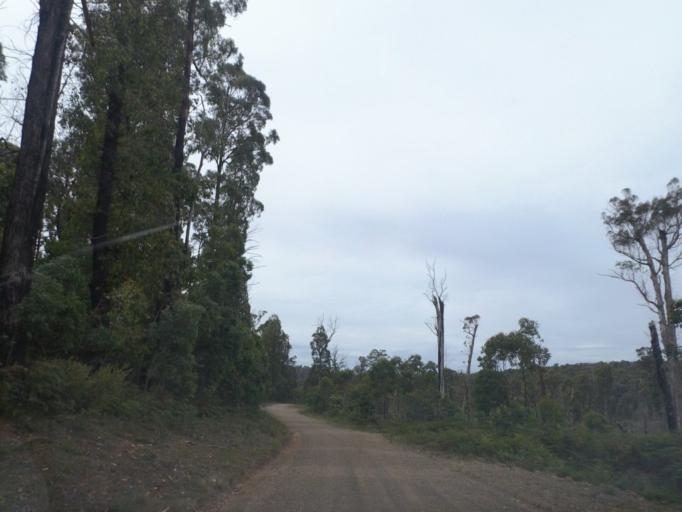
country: AU
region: Victoria
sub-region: Murrindindi
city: Alexandra
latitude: -37.4047
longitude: 145.5928
